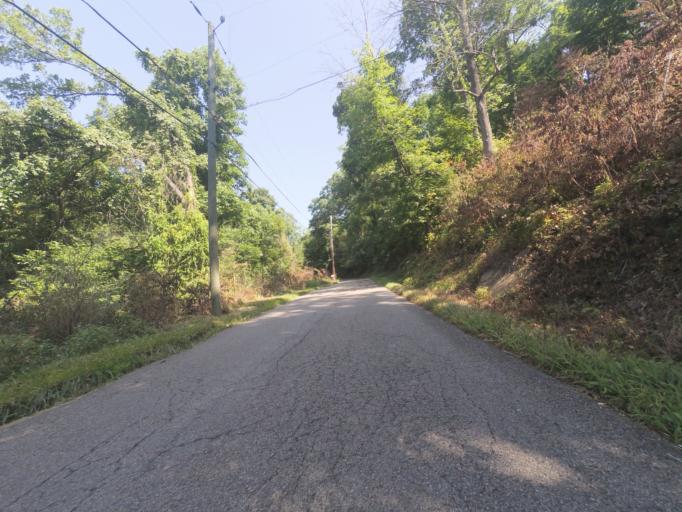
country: US
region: West Virginia
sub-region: Cabell County
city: Huntington
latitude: 38.4318
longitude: -82.4485
